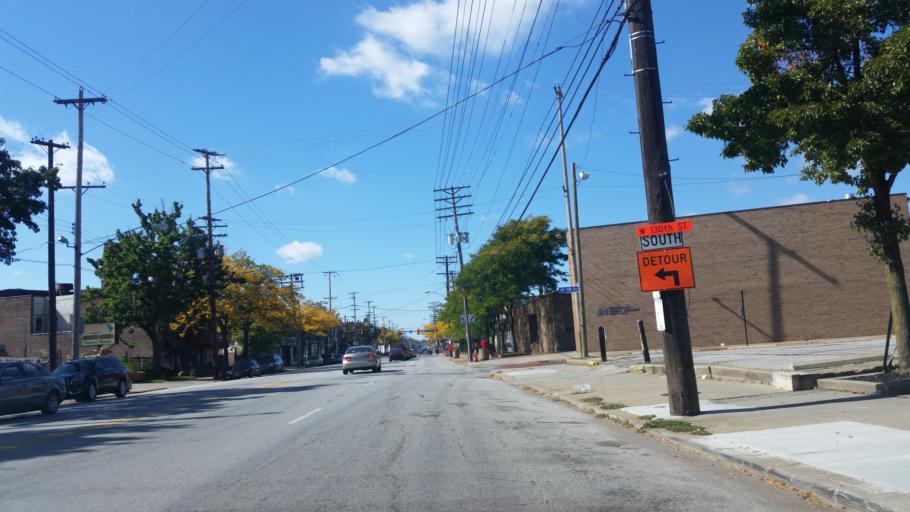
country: US
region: Ohio
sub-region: Cuyahoga County
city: Lakewood
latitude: 41.4626
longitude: -81.7671
